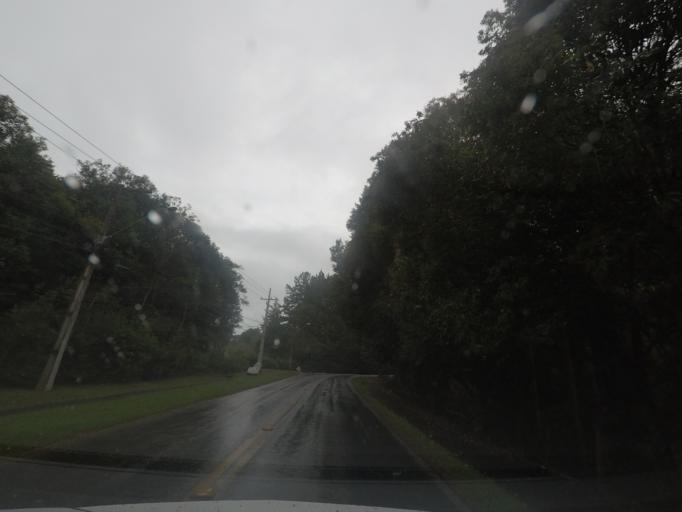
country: BR
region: Parana
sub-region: Quatro Barras
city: Quatro Barras
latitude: -25.3746
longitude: -49.1059
